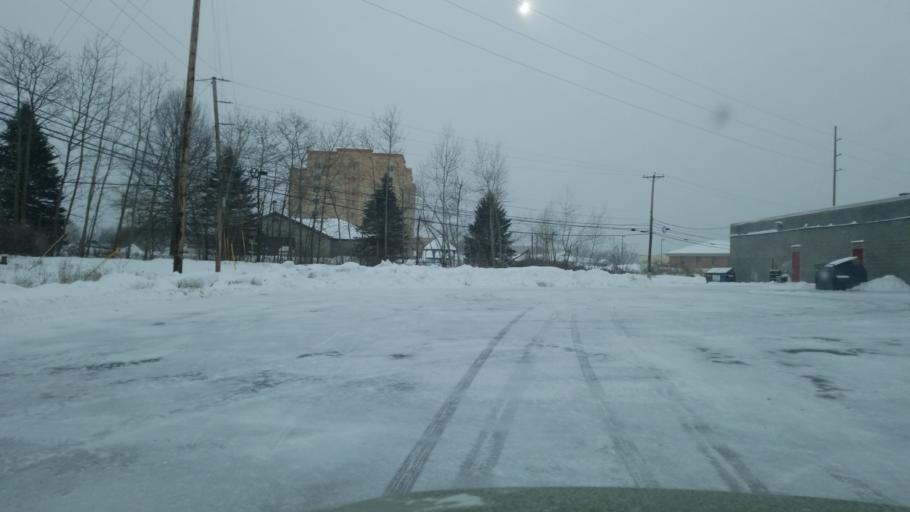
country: US
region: Pennsylvania
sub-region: Clearfield County
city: Clearfield
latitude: 41.0239
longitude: -78.4124
